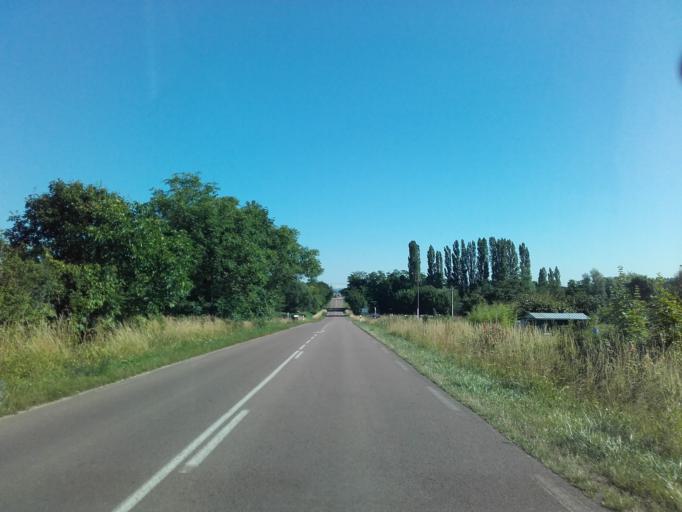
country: FR
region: Bourgogne
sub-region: Departement de Saone-et-Loire
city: Rully
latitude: 46.8728
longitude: 4.7538
